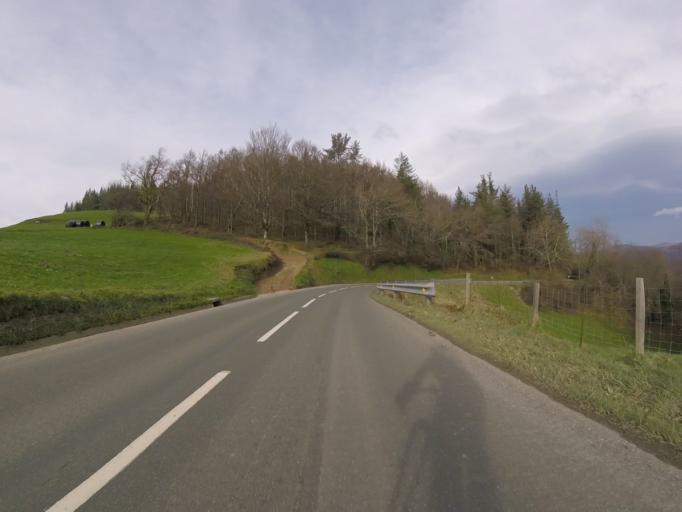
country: ES
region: Basque Country
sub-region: Provincia de Guipuzcoa
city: Beizama
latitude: 43.1563
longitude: -2.2060
